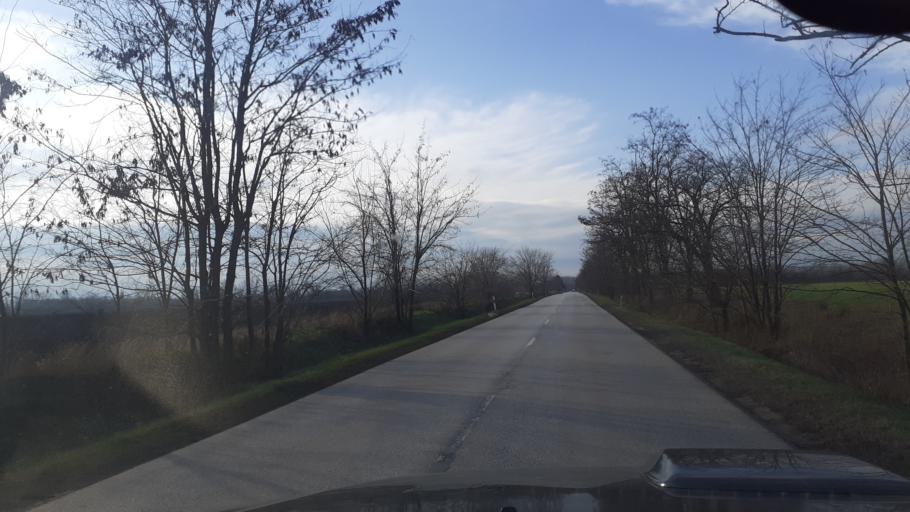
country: HU
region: Bacs-Kiskun
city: Tass
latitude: 47.0207
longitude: 19.0574
